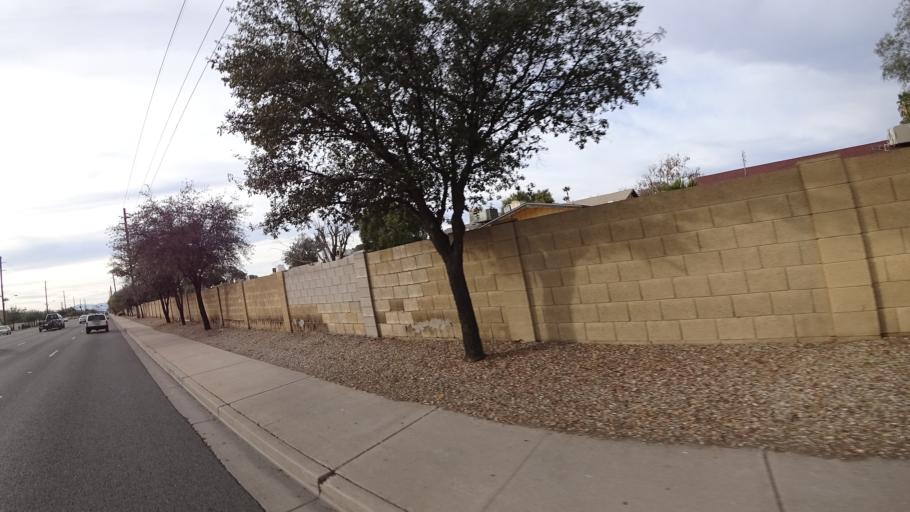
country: US
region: Arizona
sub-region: Maricopa County
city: Glendale
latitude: 33.5674
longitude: -112.1961
